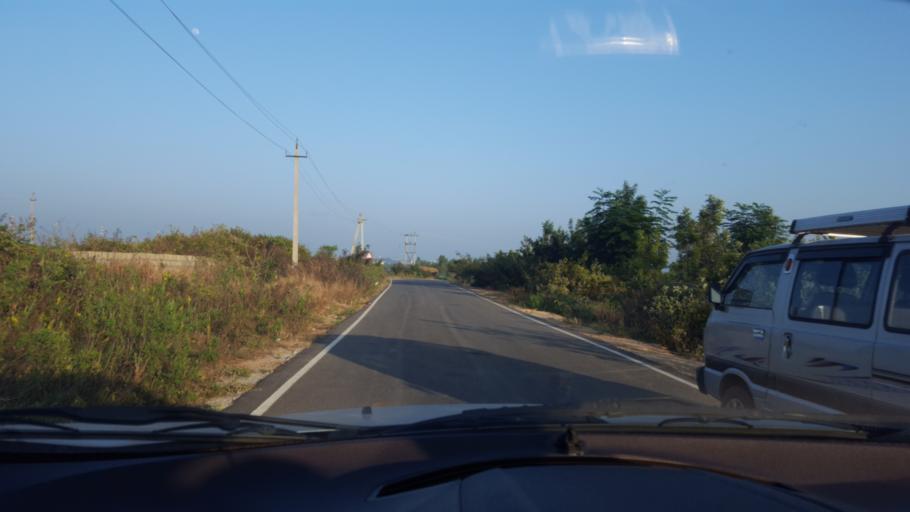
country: IN
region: Karnataka
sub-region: Bangalore Urban
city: Yelahanka
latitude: 13.1897
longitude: 77.6034
